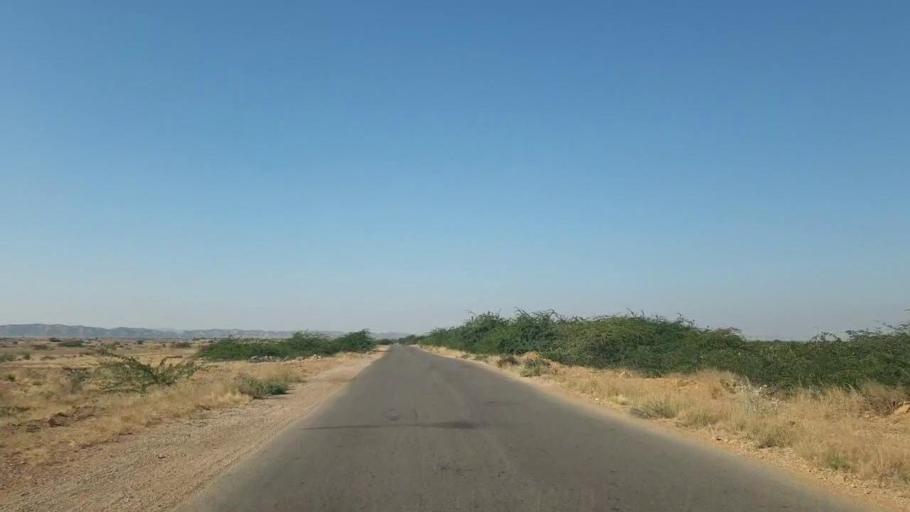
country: PK
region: Sindh
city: Malir Cantonment
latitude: 25.2703
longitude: 67.5932
